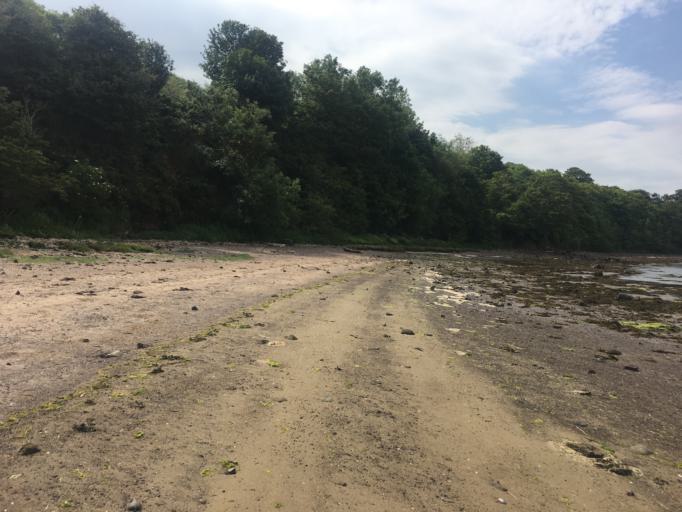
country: GB
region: England
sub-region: Northumberland
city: Bamburgh
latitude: 55.6093
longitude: -1.7586
